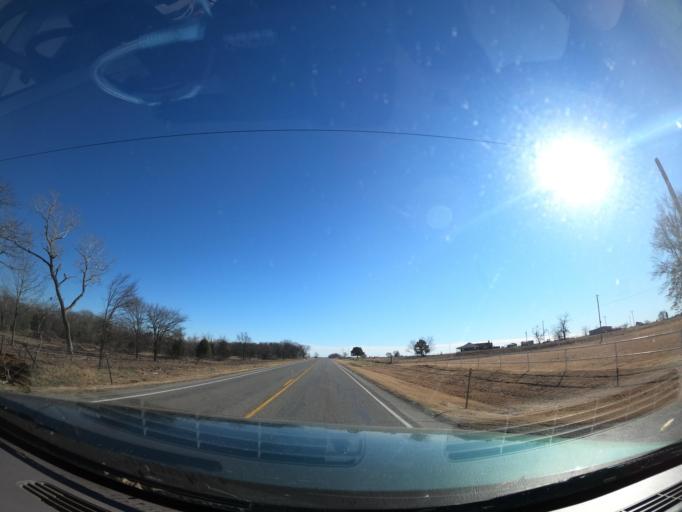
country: US
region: Oklahoma
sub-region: Muskogee County
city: Haskell
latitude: 35.7641
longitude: -95.6491
